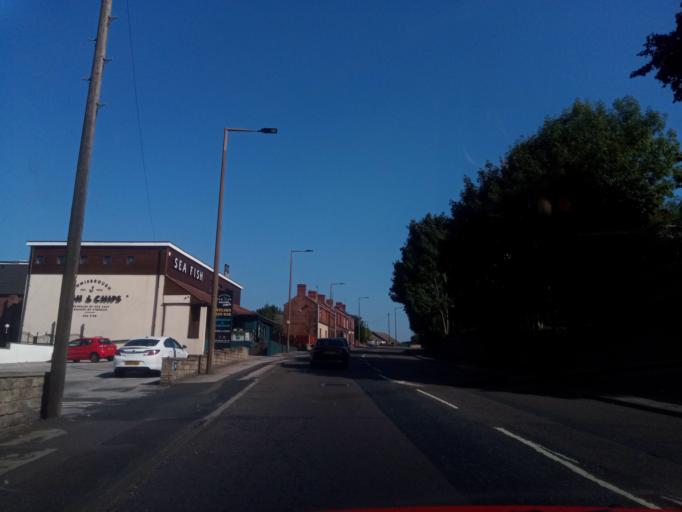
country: GB
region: England
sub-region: Doncaster
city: Conisbrough
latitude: 53.4814
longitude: -1.2251
